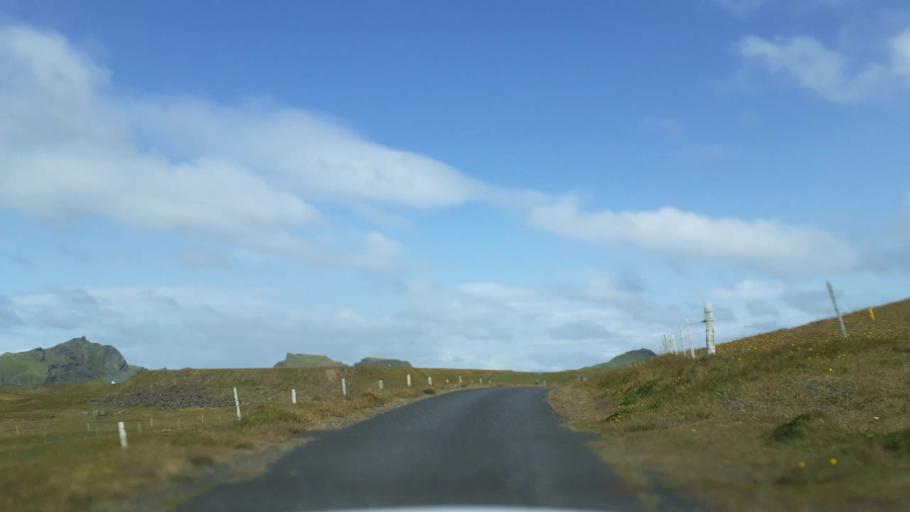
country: IS
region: South
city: Vestmannaeyjar
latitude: 63.4180
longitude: -20.2813
